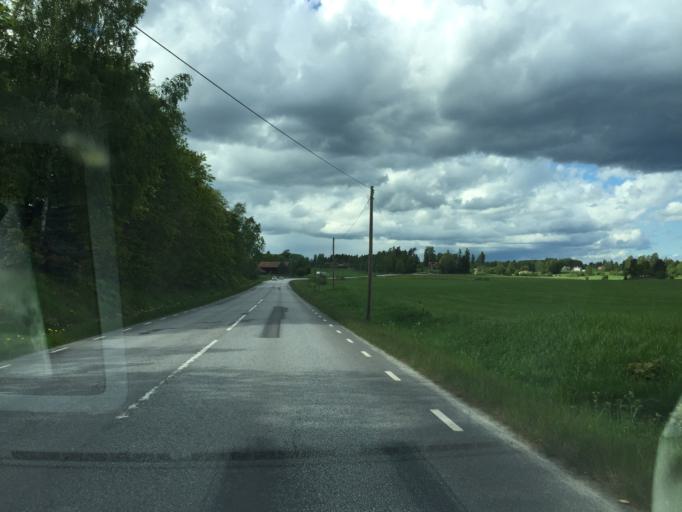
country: SE
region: OEstergoetland
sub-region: Finspangs Kommun
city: Finspang
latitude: 58.6698
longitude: 15.7597
